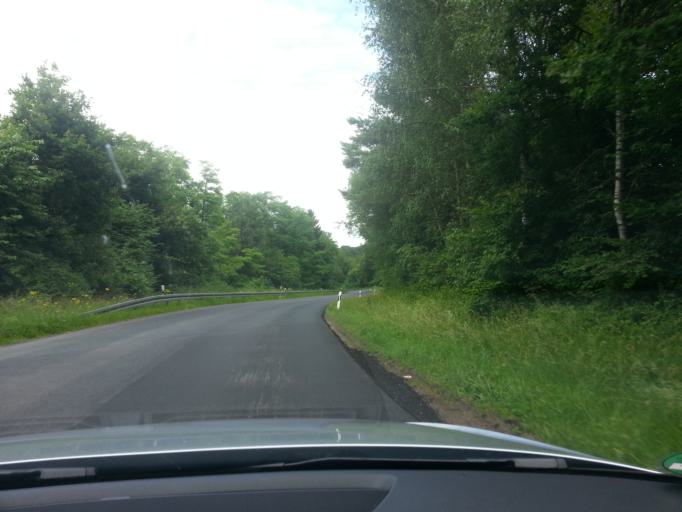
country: DE
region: Saarland
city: Orscholz
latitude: 49.4791
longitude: 6.4940
